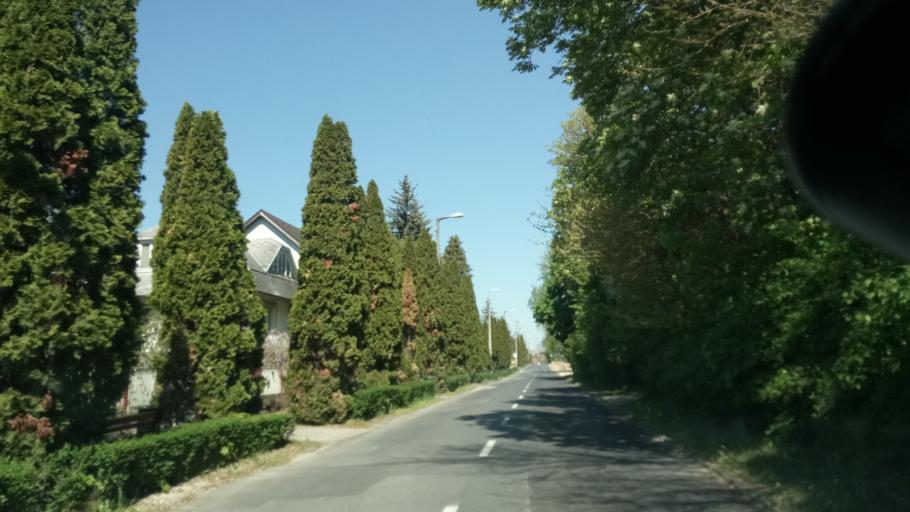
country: HU
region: Zala
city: Heviz
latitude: 46.7831
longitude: 17.1878
